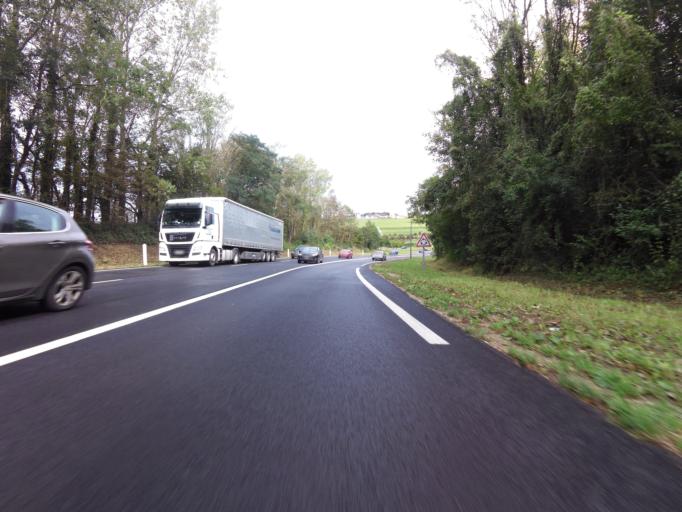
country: FR
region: Haute-Normandie
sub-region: Departement de la Seine-Maritime
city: Criel-sur-Mer
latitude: 50.0196
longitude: 1.3232
